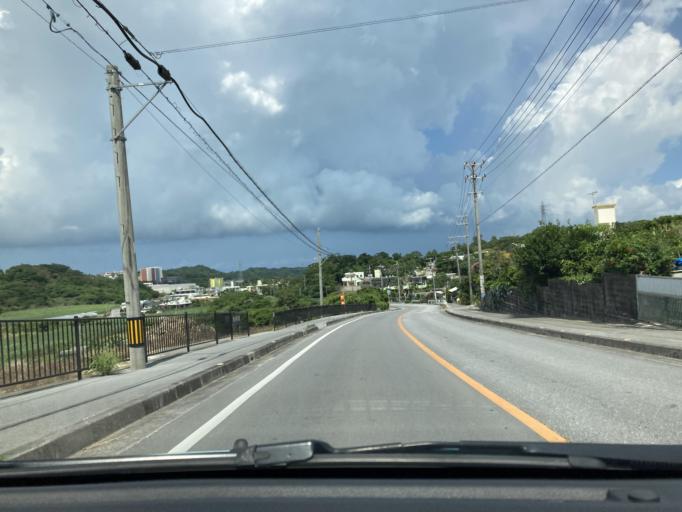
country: JP
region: Okinawa
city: Tomigusuku
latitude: 26.1589
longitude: 127.7782
